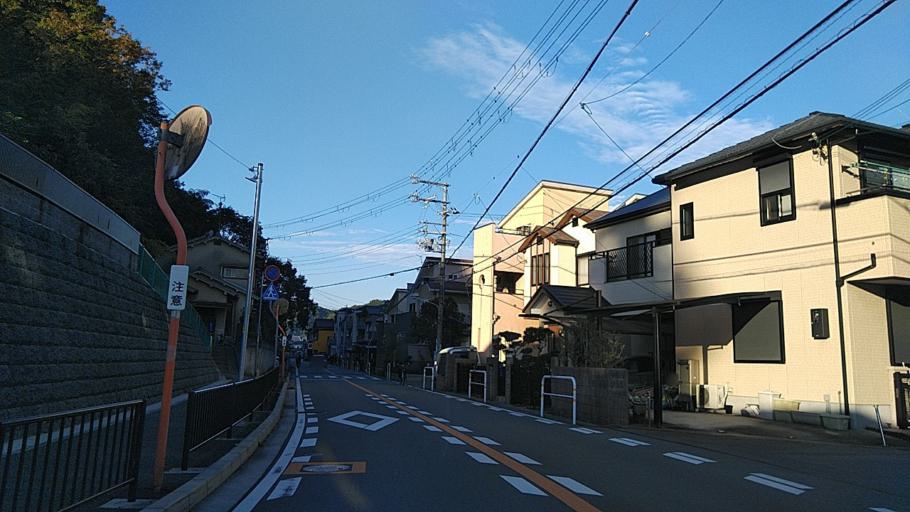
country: JP
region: Osaka
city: Ikeda
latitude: 34.8879
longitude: 135.4050
